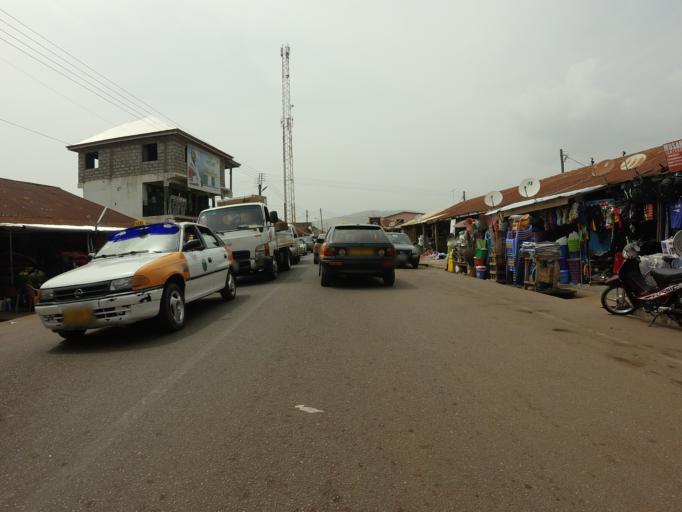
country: GH
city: Akropong
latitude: 6.1048
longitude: -0.0140
